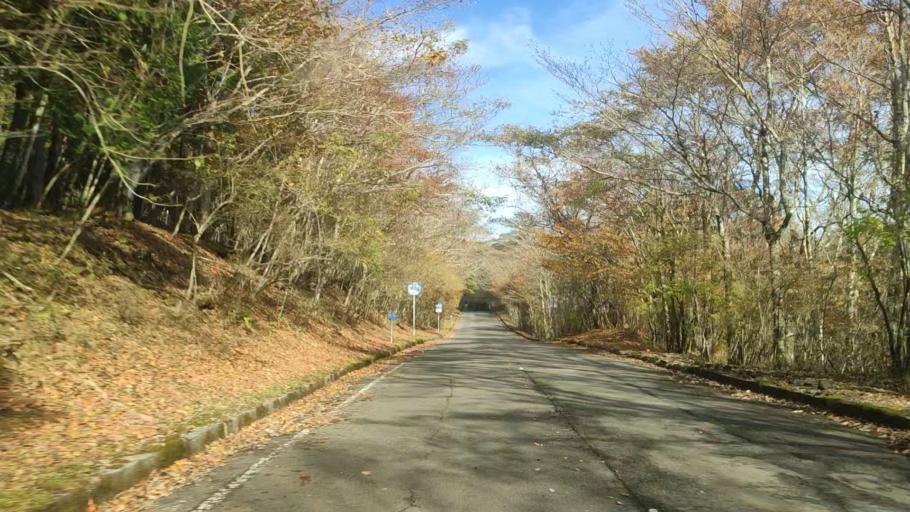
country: JP
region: Shizuoka
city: Fujinomiya
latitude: 35.3014
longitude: 138.7226
